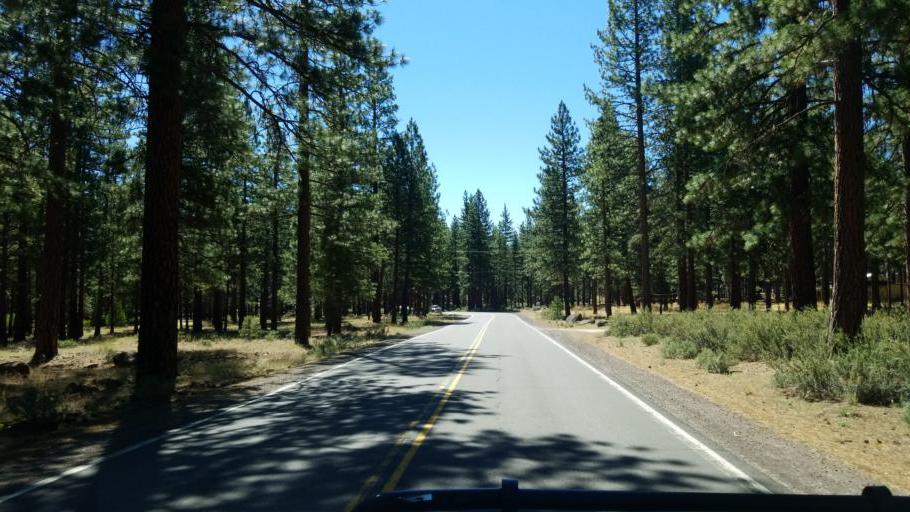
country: US
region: California
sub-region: Lassen County
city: Susanville
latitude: 40.4238
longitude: -120.7218
